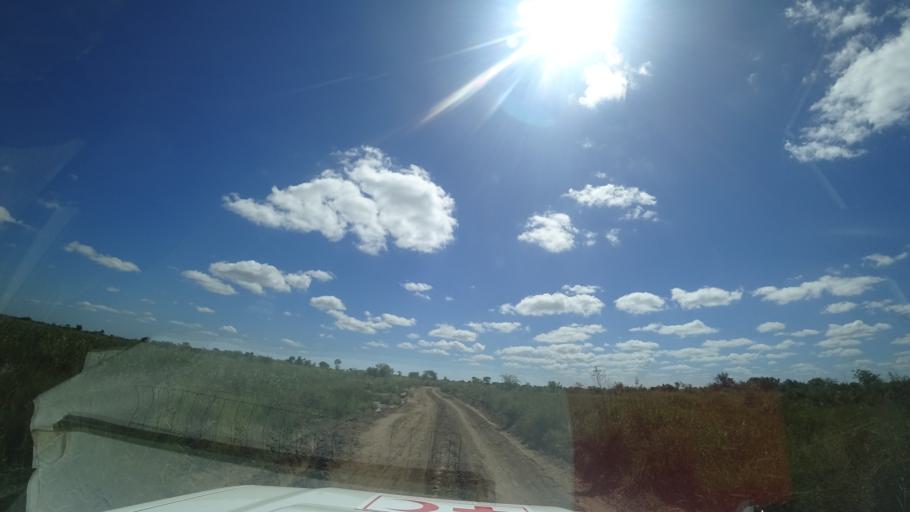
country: MZ
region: Sofala
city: Dondo
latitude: -19.4671
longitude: 34.5973
